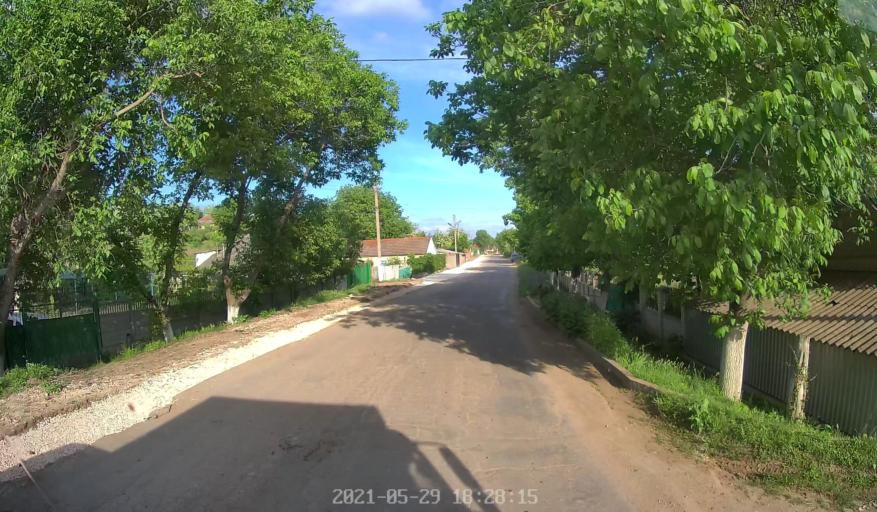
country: MD
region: Chisinau
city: Singera
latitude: 46.8292
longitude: 28.8653
